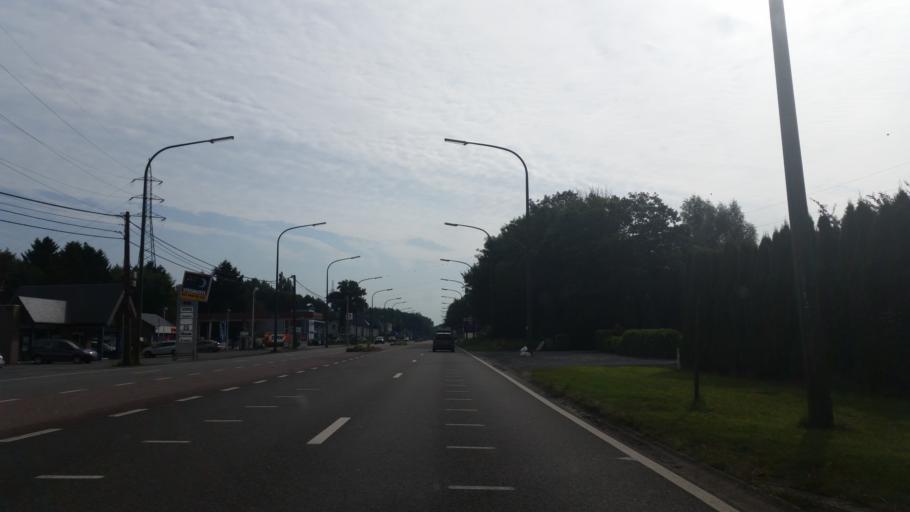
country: BE
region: Wallonia
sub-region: Province de Liege
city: Seraing
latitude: 50.5420
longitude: 5.4756
